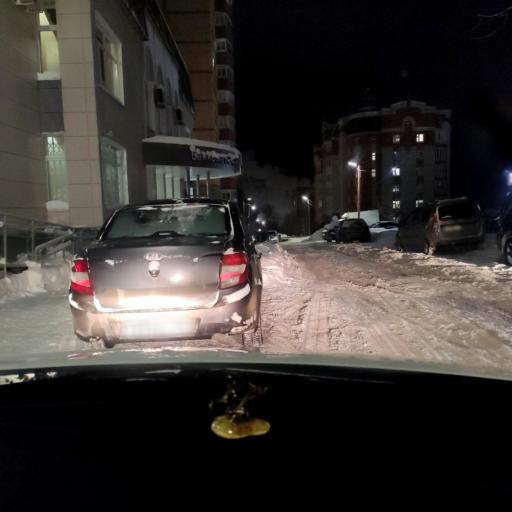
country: RU
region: Tatarstan
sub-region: Zelenodol'skiy Rayon
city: Zelenodolsk
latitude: 55.8457
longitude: 48.4947
